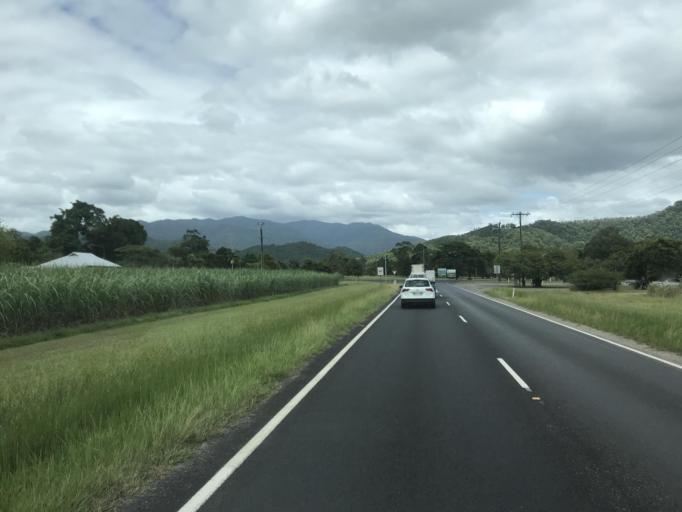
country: AU
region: Queensland
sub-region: Cassowary Coast
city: Innisfail
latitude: -17.8093
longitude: 146.0082
